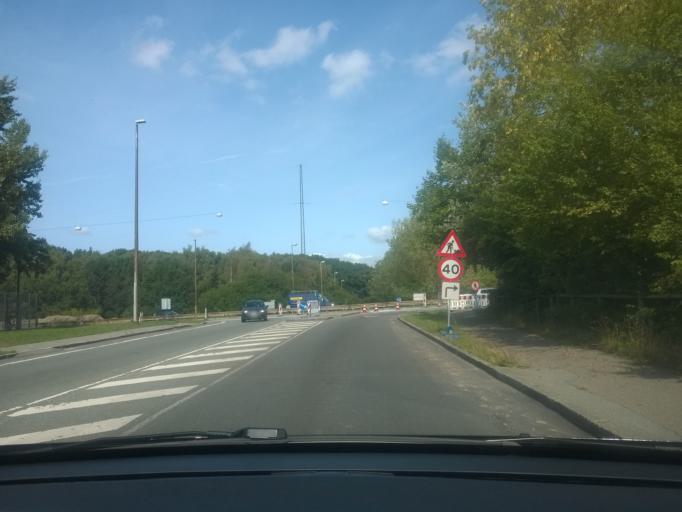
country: DK
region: Capital Region
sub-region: Herlev Kommune
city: Herlev
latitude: 55.7063
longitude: 12.4249
